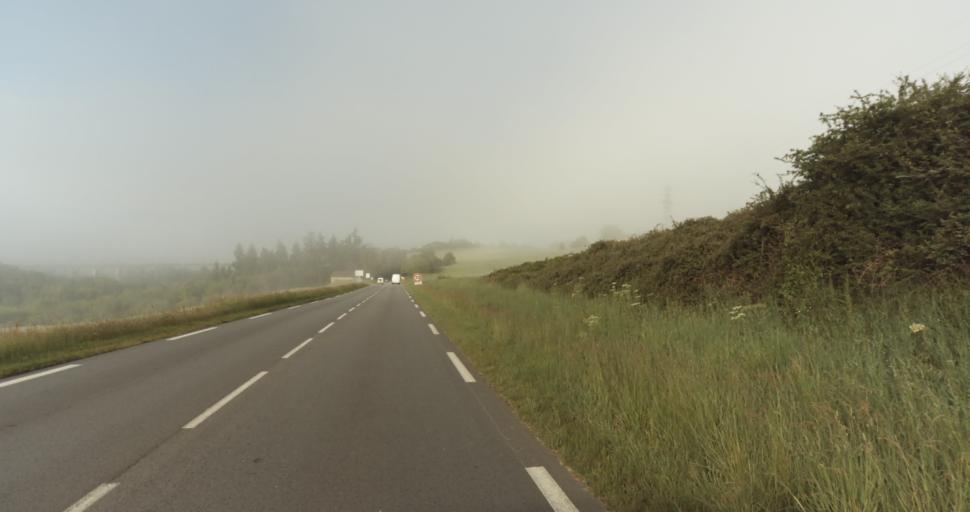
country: FR
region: Limousin
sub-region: Departement de la Haute-Vienne
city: Le Vigen
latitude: 45.7597
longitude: 1.2931
